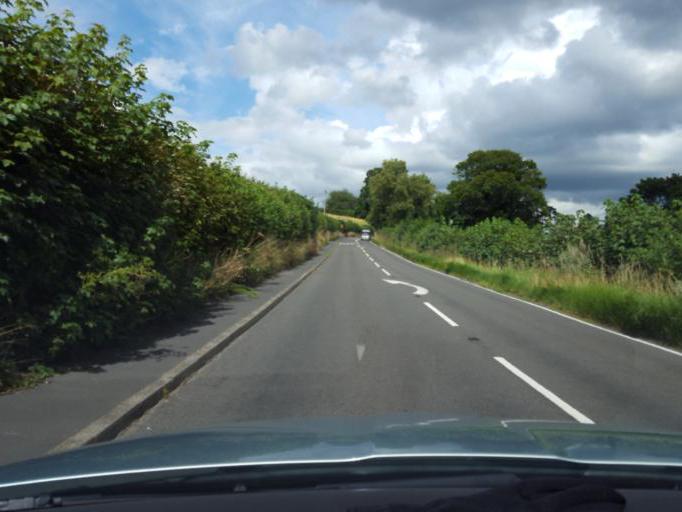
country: GB
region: Wales
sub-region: Wrexham
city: Chirk
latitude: 52.9704
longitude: -3.1038
